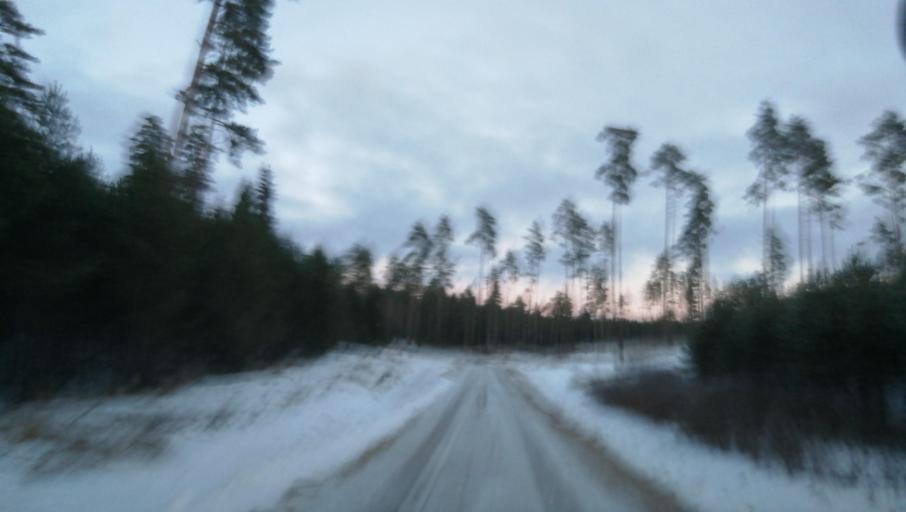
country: LV
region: Amatas Novads
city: Drabesi
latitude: 57.2148
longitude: 25.2848
